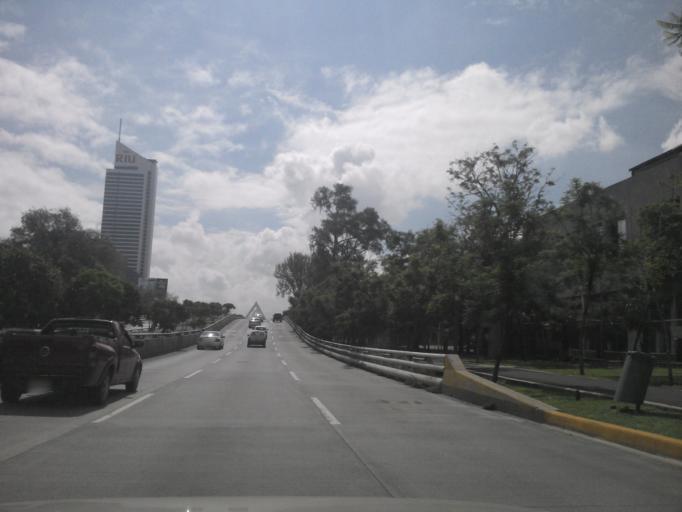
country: MX
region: Jalisco
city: Guadalajara
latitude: 20.6676
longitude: -103.3989
